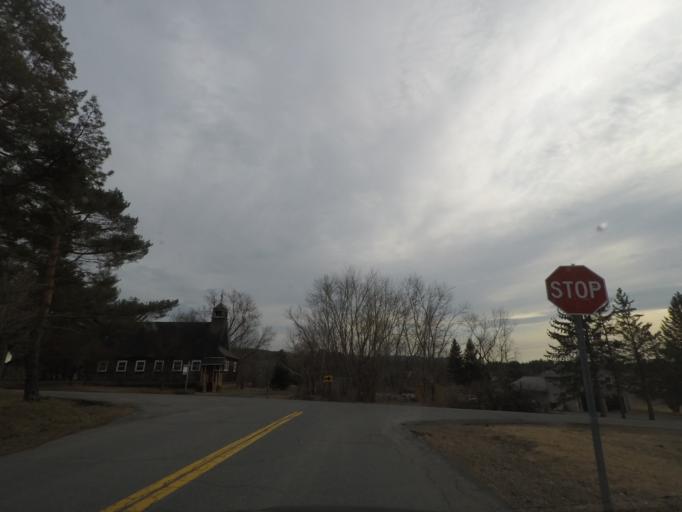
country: US
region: New York
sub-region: Rensselaer County
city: Hoosick Falls
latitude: 42.8455
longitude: -73.4563
